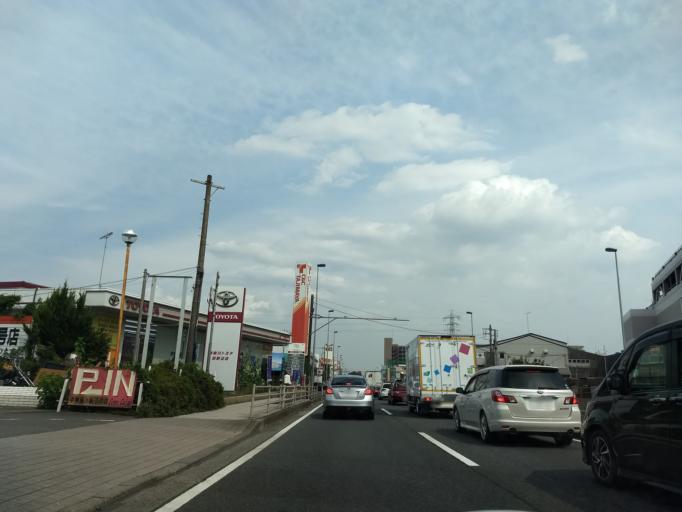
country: JP
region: Tokyo
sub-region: Machida-shi
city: Machida
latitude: 35.5562
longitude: 139.4101
